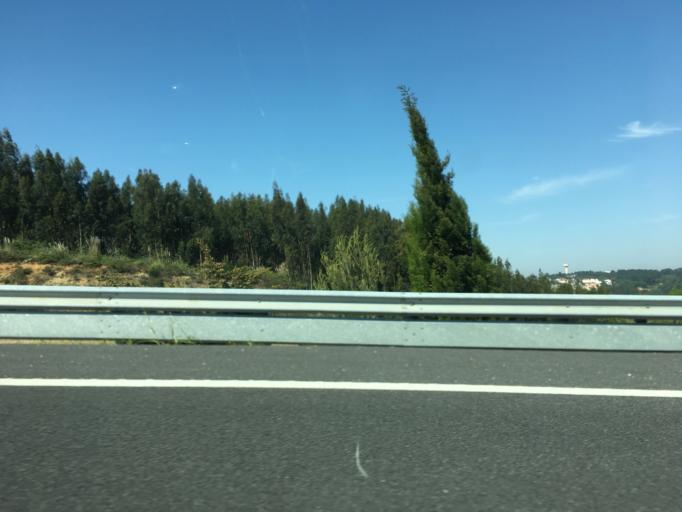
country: PT
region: Lisbon
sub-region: Sintra
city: Cacem
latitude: 38.7936
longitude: -9.3069
